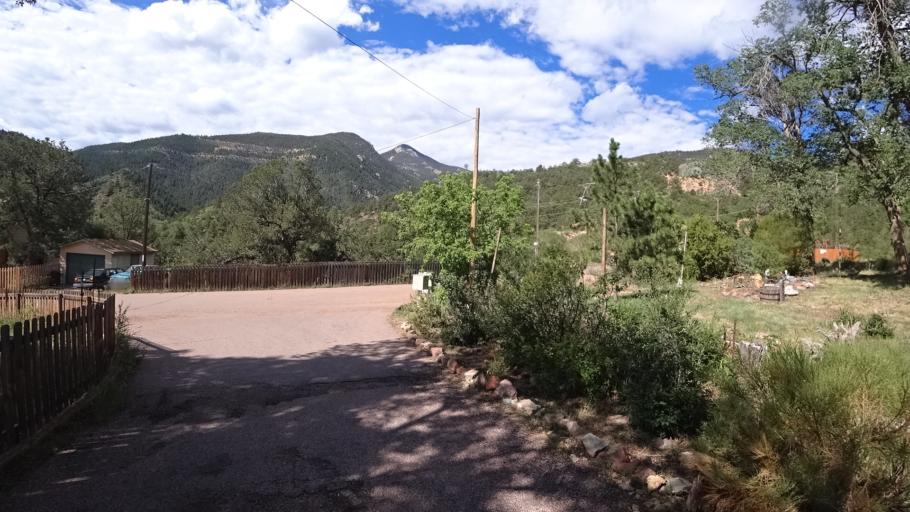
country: US
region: Colorado
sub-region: El Paso County
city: Manitou Springs
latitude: 38.8619
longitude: -104.9255
